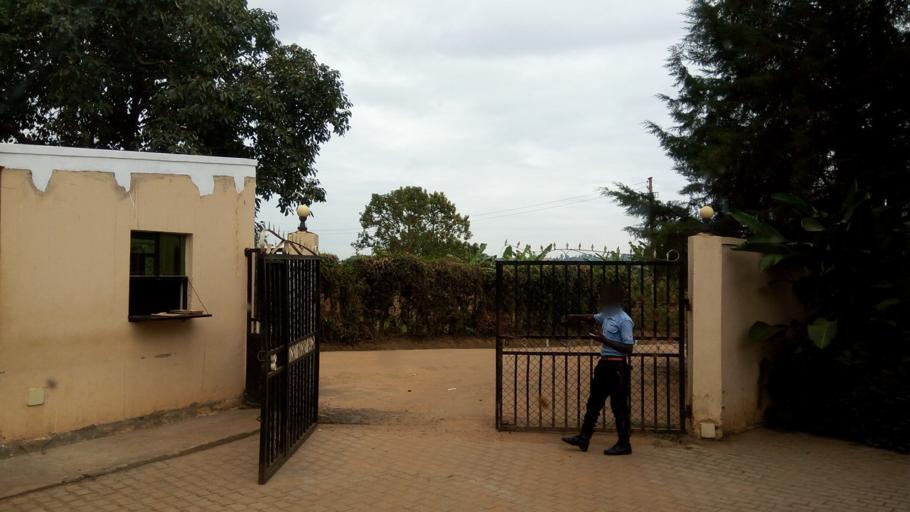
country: UG
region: Western Region
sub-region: Mbarara District
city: Bwizibwera
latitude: -0.6065
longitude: 30.6301
